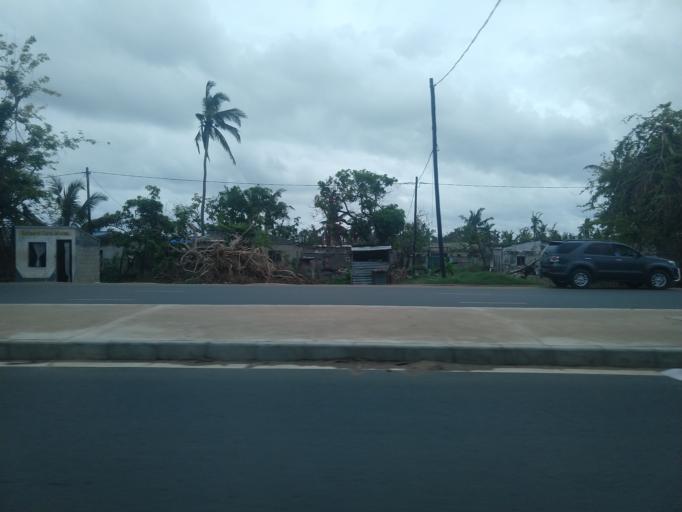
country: MZ
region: Sofala
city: Beira
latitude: -19.7857
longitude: 34.8762
